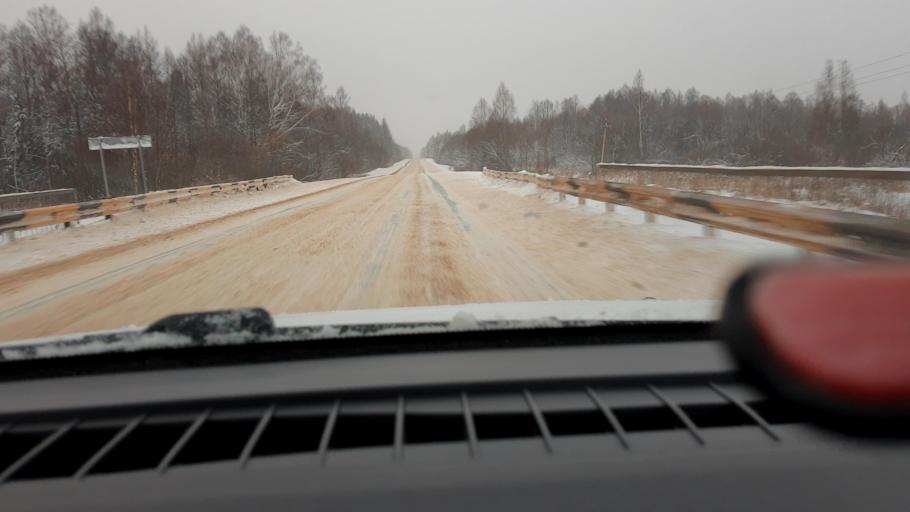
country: RU
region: Nizjnij Novgorod
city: Sharanga
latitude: 57.2203
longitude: 46.5019
